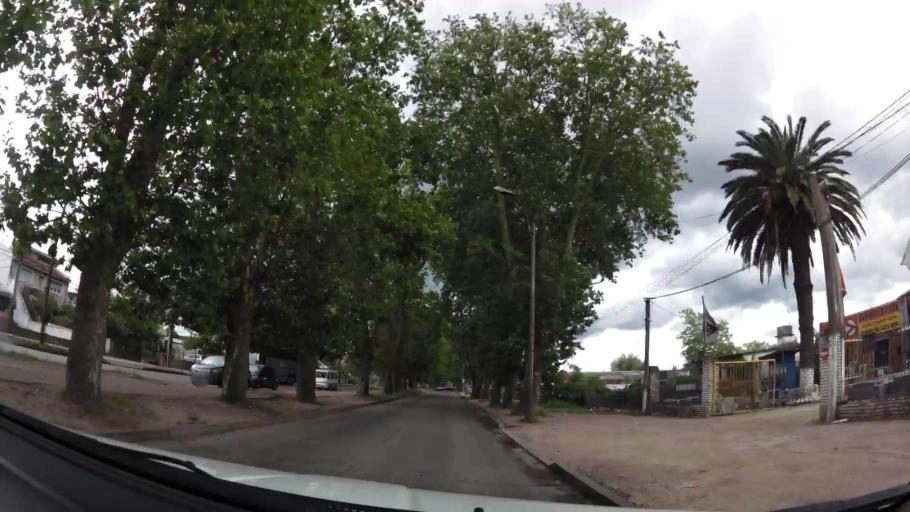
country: UY
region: Canelones
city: Toledo
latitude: -34.8129
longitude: -56.1383
